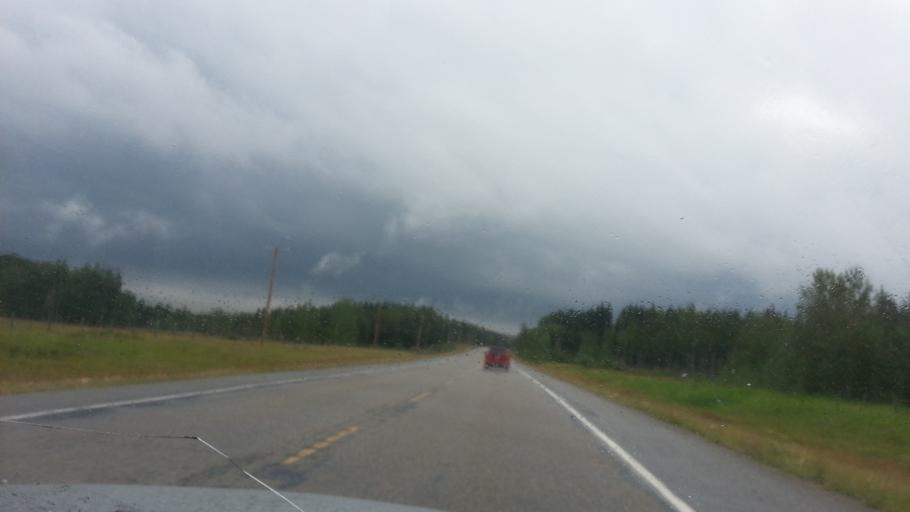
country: CA
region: Alberta
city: Cochrane
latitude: 50.9214
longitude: -114.5781
